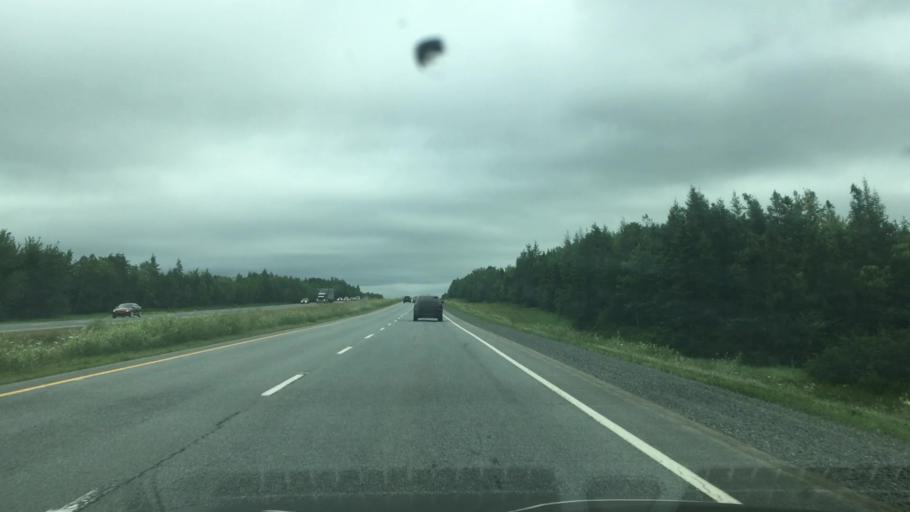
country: CA
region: Nova Scotia
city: Cole Harbour
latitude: 44.9990
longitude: -63.4888
